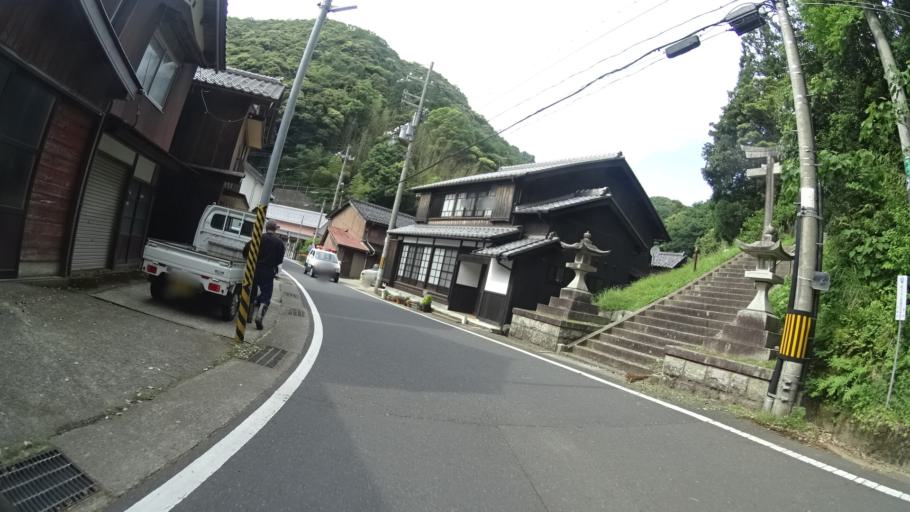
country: JP
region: Kyoto
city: Miyazu
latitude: 35.6694
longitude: 135.2801
